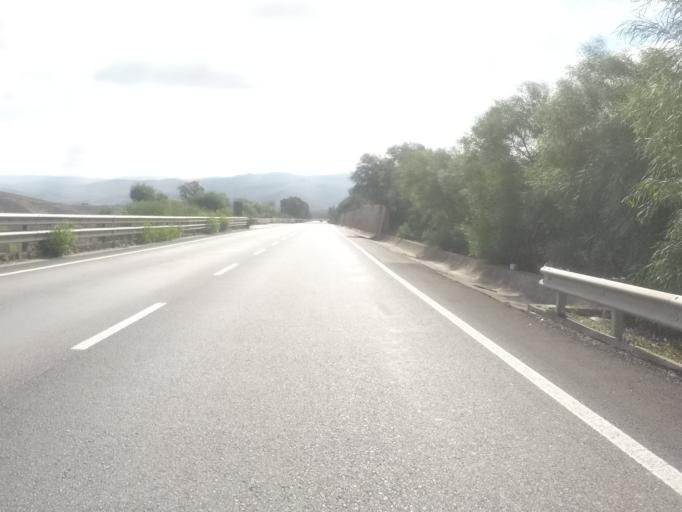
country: IT
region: Sicily
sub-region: Provincia di Caltanissetta
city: Caltanissetta
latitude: 37.4733
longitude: 14.0910
